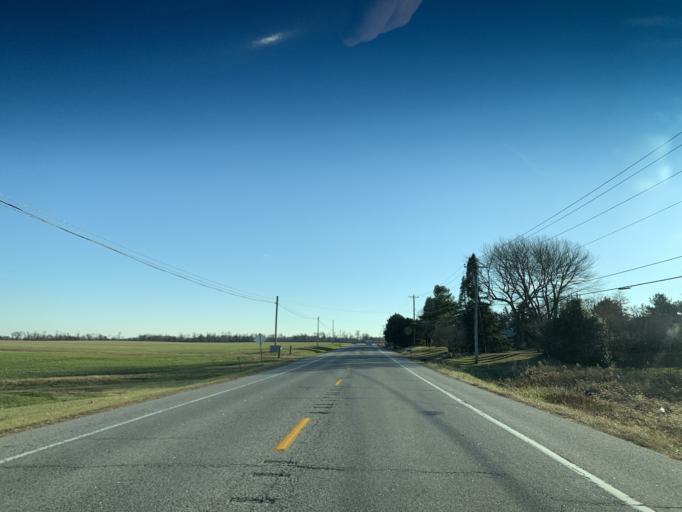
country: US
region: Delaware
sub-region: New Castle County
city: Middletown
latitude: 39.3947
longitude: -75.8710
